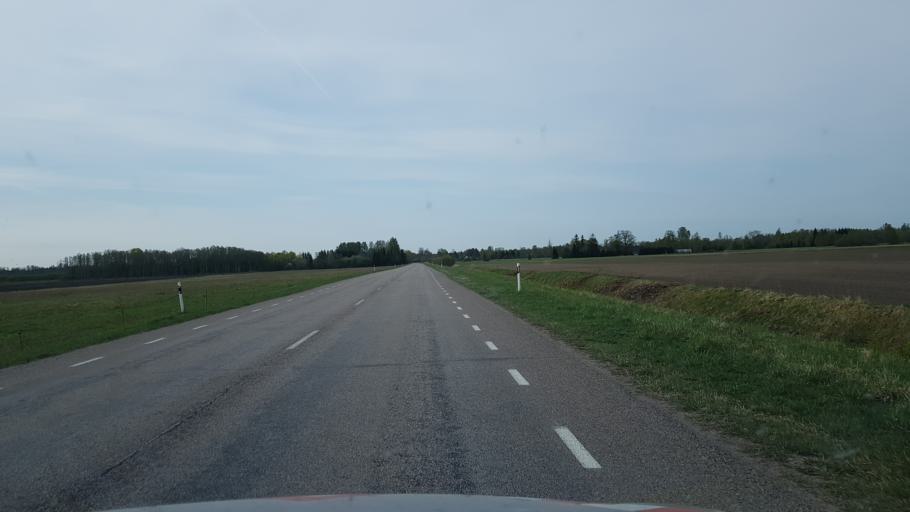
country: EE
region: Paernumaa
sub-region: Audru vald
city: Audru
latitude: 58.3789
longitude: 24.2711
